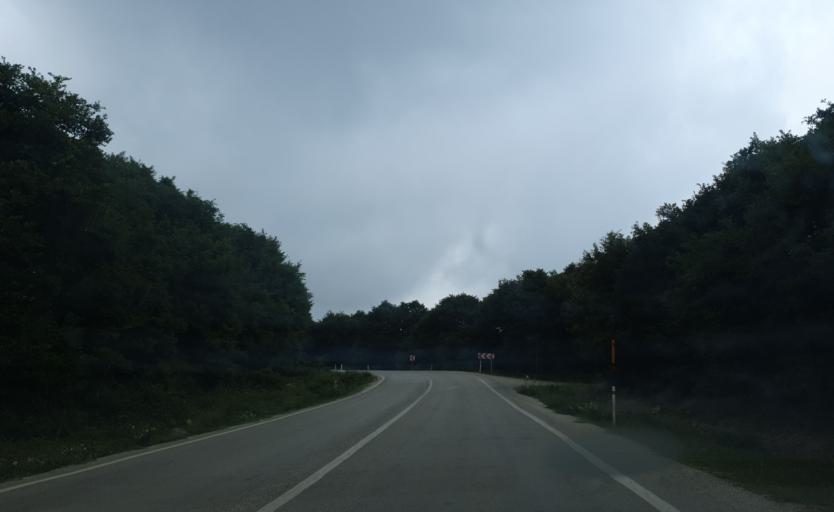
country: TR
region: Kirklareli
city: Salmydessus
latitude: 41.5711
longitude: 28.0796
